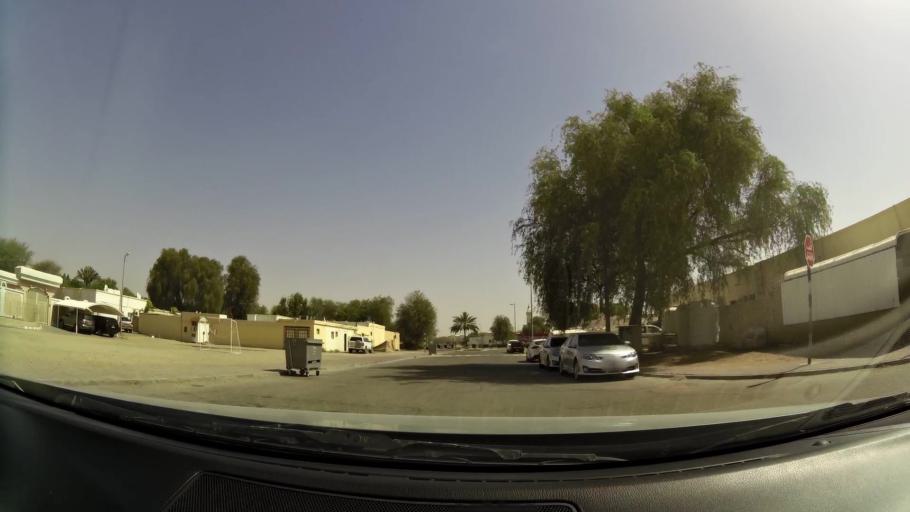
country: OM
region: Al Buraimi
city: Al Buraymi
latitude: 24.2959
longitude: 55.7774
